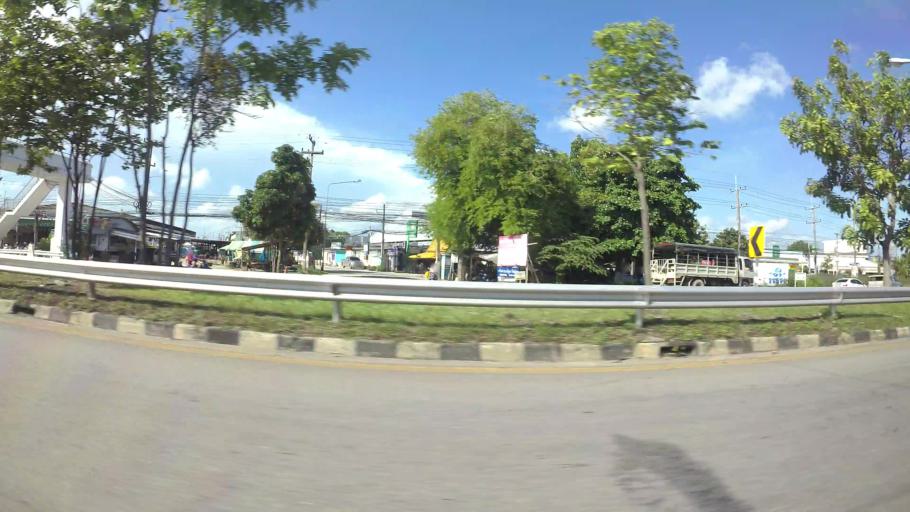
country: TH
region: Rayong
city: Rayong
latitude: 12.6657
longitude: 101.2980
